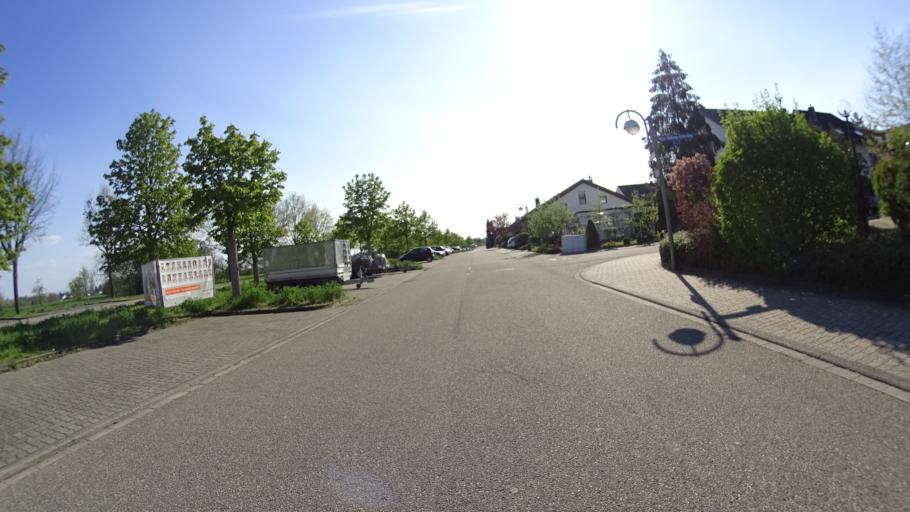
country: DE
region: Baden-Wuerttemberg
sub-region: Karlsruhe Region
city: Karlsruhe
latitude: 49.0436
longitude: 8.3823
